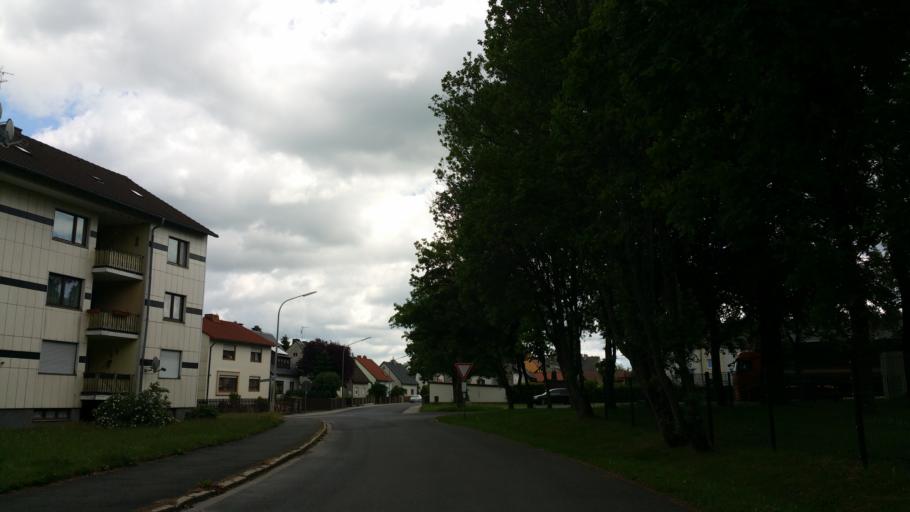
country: DE
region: Bavaria
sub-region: Upper Franconia
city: Kirchenlamitz
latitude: 50.1578
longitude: 11.9442
